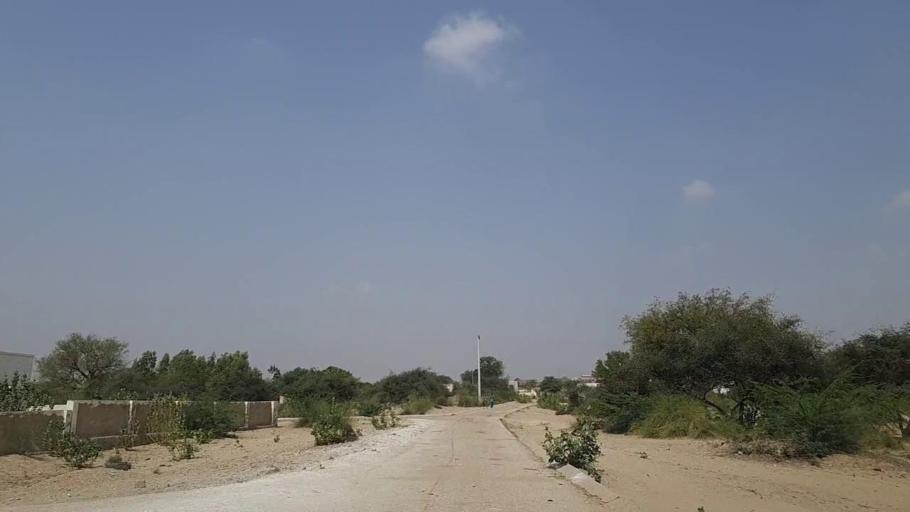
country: PK
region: Sindh
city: Mithi
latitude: 24.7623
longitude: 69.9260
